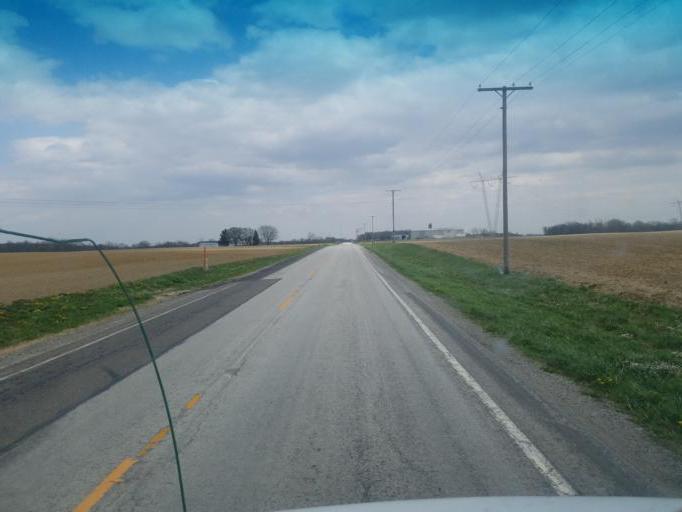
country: US
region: Ohio
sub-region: Wyandot County
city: Upper Sandusky
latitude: 40.9493
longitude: -83.2155
